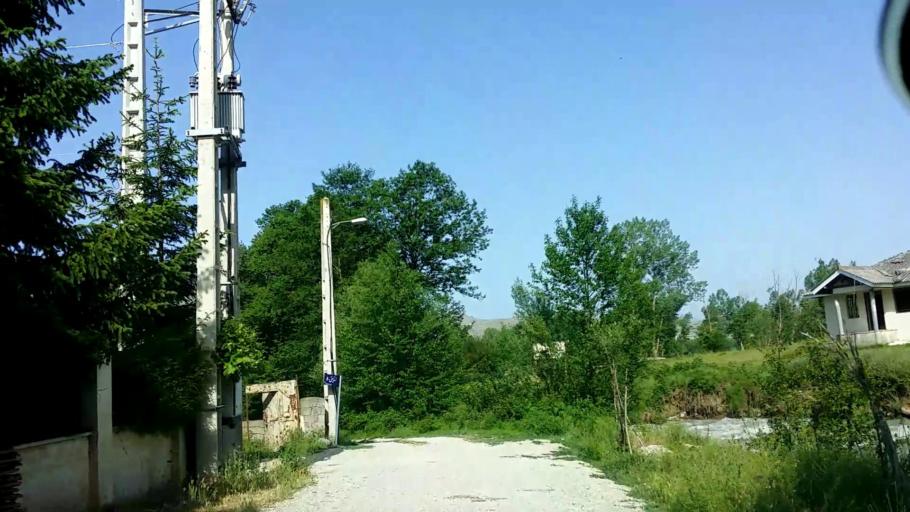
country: IR
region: Mazandaran
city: `Abbasabad
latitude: 36.5281
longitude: 51.1841
